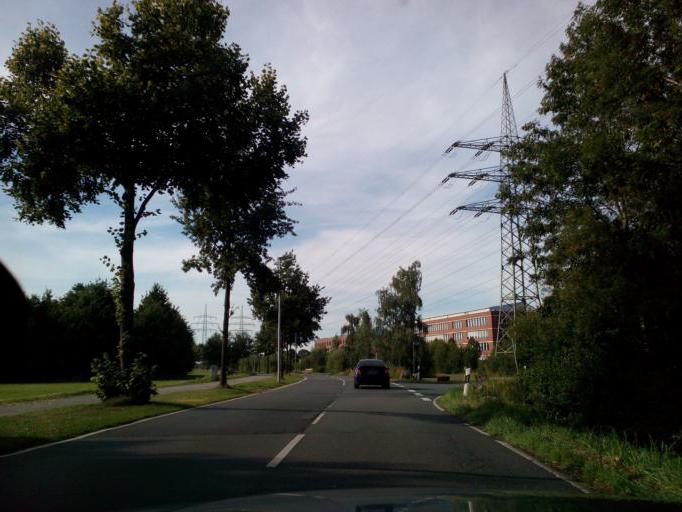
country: DE
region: North Rhine-Westphalia
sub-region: Regierungsbezirk Munster
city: Muenster
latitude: 51.9310
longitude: 7.5887
